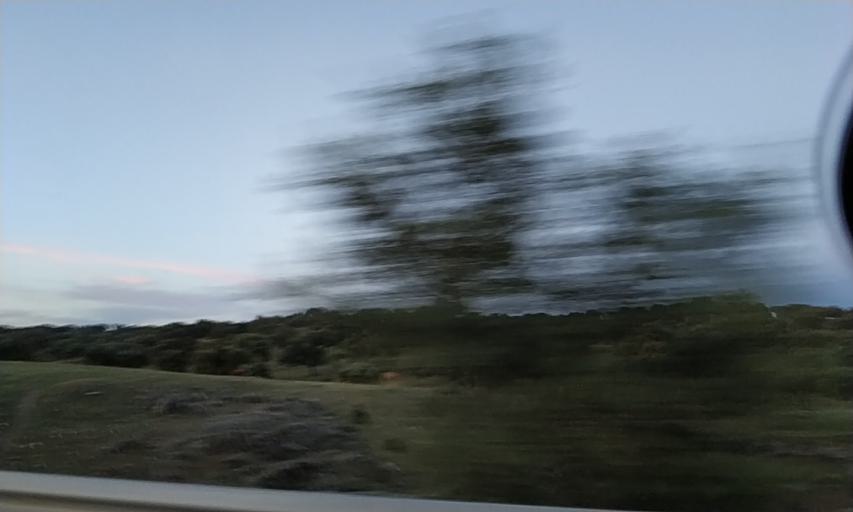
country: ES
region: Extremadura
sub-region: Provincia de Caceres
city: Piedras Albas
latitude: 39.7691
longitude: -6.9135
